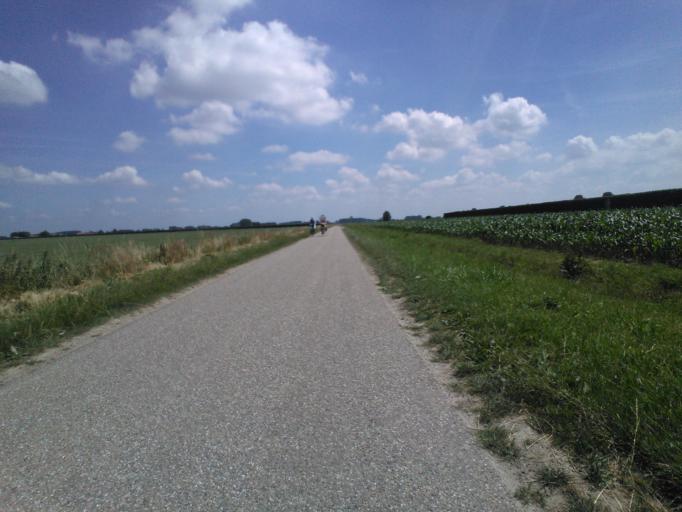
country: NL
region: North Brabant
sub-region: Gemeente Waalwijk
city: Waspik
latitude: 51.7240
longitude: 4.9209
